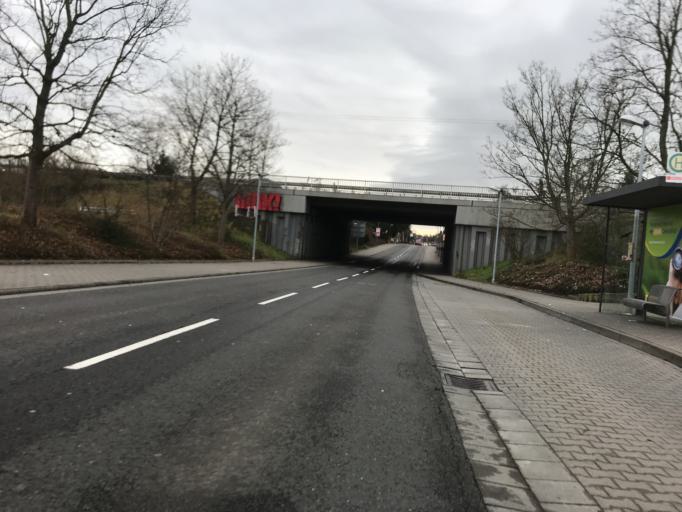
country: DE
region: Rheinland-Pfalz
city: Ingelheim am Rhein
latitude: 49.9814
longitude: 8.0320
